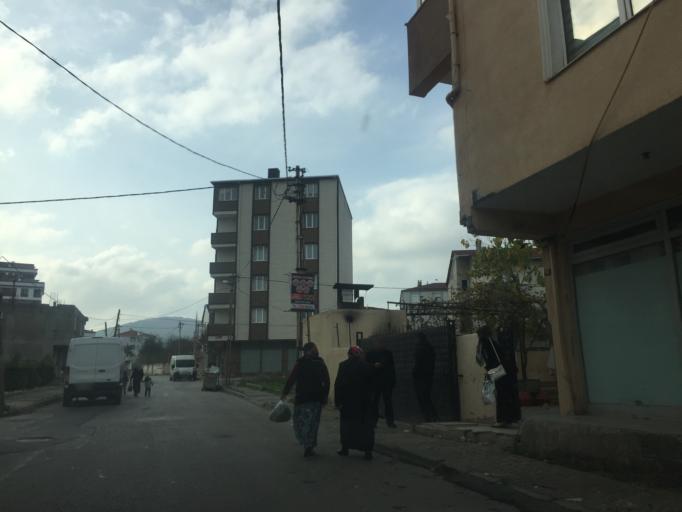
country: TR
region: Istanbul
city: Sultanbeyli
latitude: 40.9392
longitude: 29.2940
